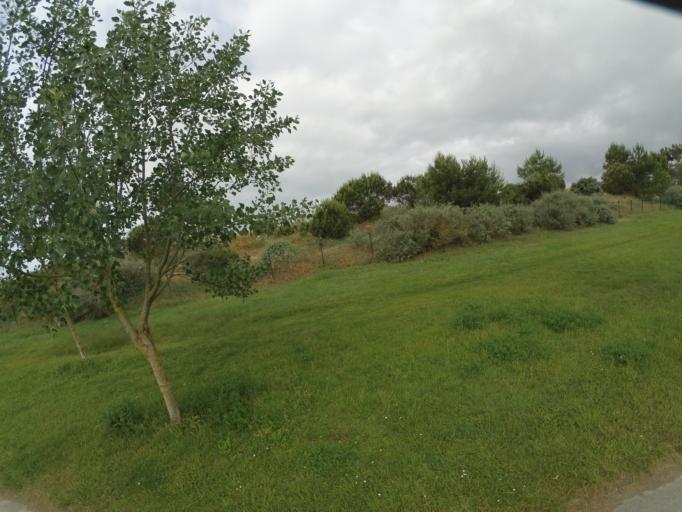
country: FR
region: Poitou-Charentes
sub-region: Departement de la Charente-Maritime
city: Angoulins
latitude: 46.1163
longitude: -1.1232
